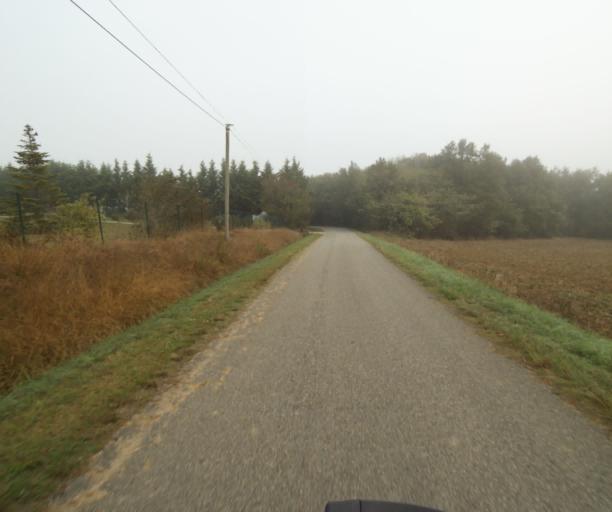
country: FR
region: Midi-Pyrenees
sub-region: Departement du Tarn-et-Garonne
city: Nohic
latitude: 43.9297
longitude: 1.4652
